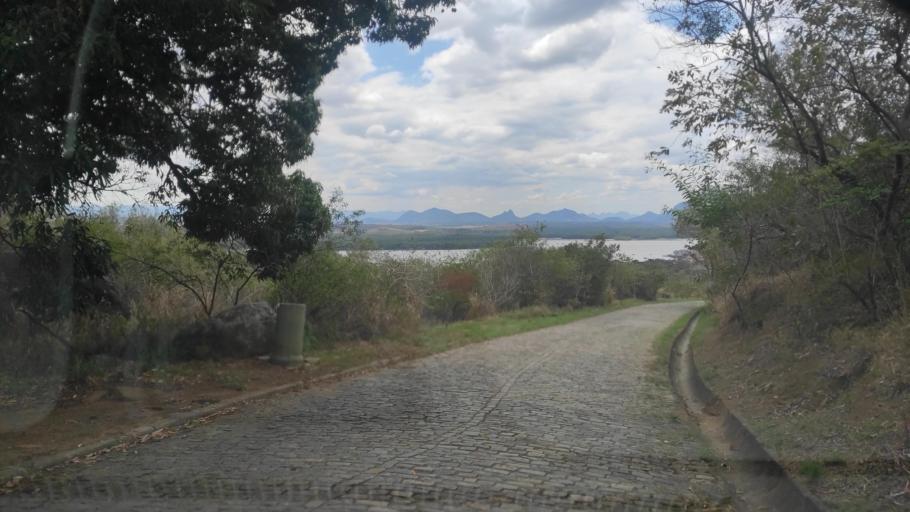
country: BR
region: Espirito Santo
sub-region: Vitoria
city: Vitoria
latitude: -20.2926
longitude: -40.3380
